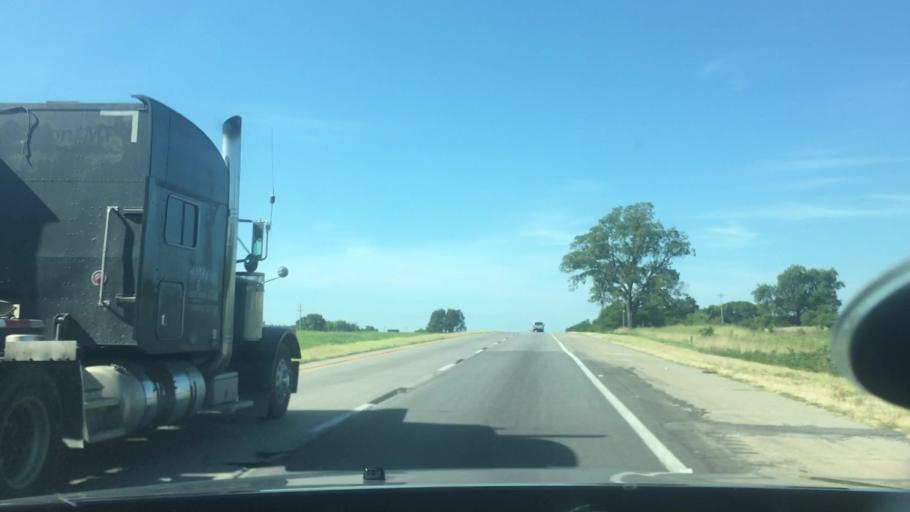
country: US
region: Oklahoma
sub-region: Bryan County
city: Durant
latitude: 34.1798
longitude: -96.2488
